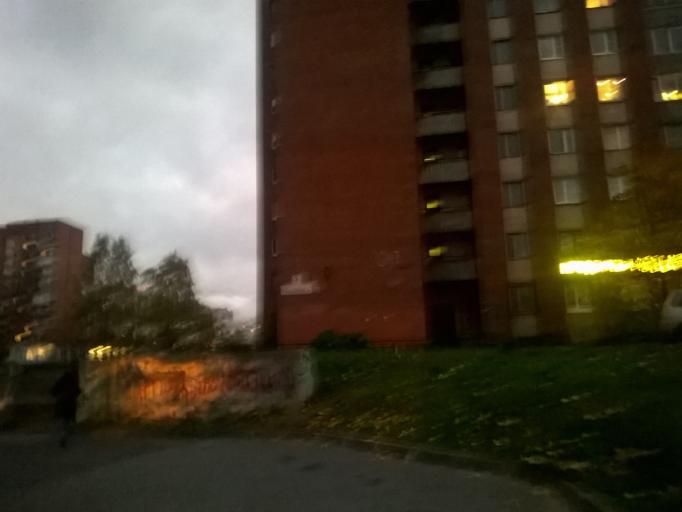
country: RU
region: St.-Petersburg
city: Ozerki
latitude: 60.0343
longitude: 30.3238
